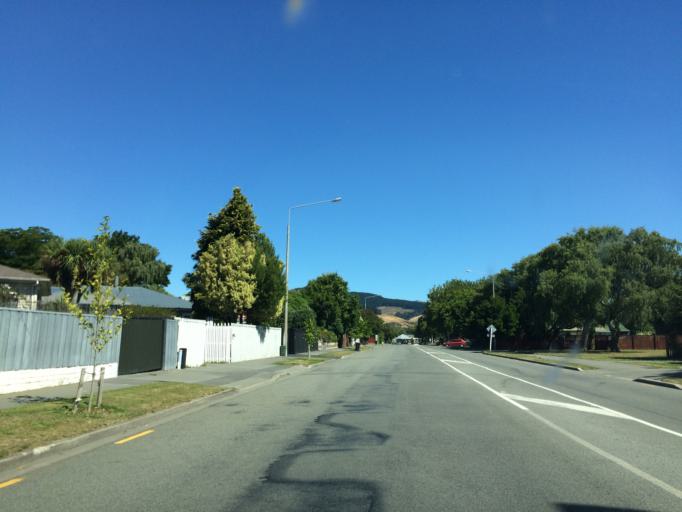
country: NZ
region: Canterbury
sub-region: Christchurch City
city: Christchurch
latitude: -43.5644
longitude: 172.6147
